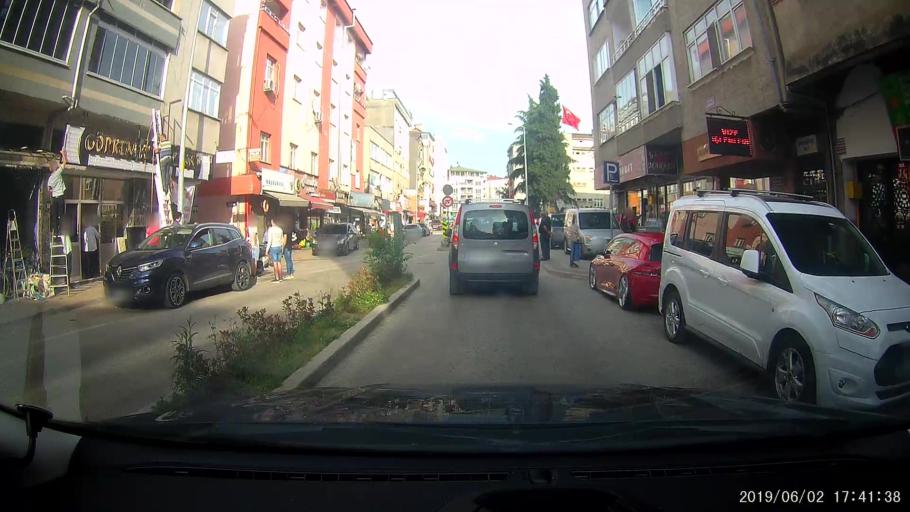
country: TR
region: Samsun
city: Terme
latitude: 41.2100
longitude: 36.9703
